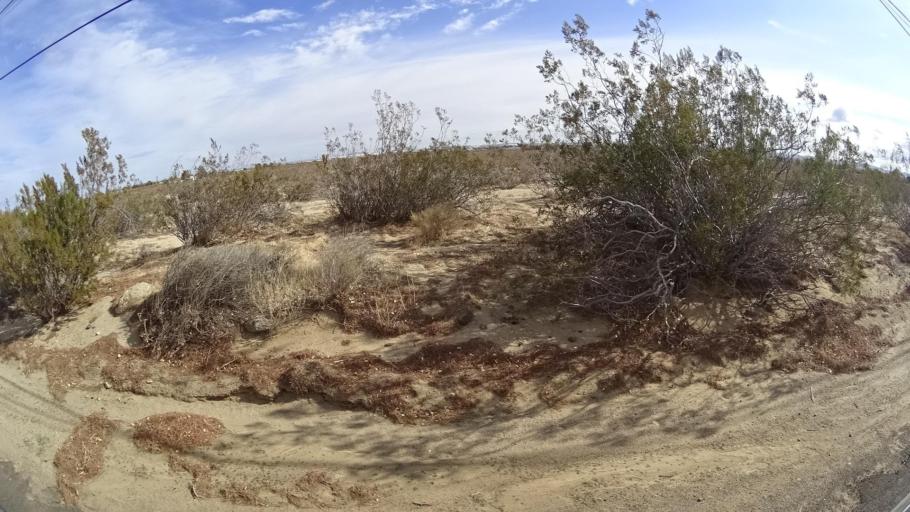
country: US
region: California
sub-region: Kern County
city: Mojave
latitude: 35.0579
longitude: -118.1946
